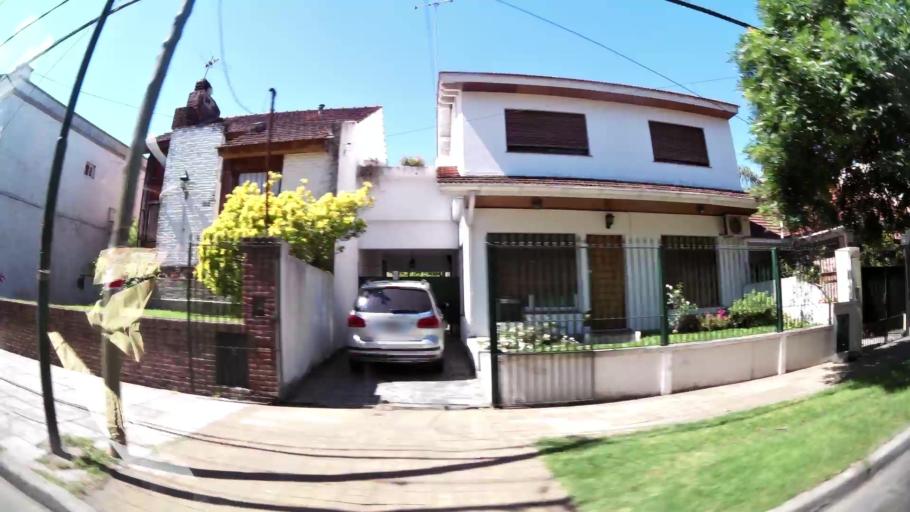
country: AR
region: Buenos Aires
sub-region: Partido de San Isidro
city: San Isidro
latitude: -34.4654
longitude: -58.5076
